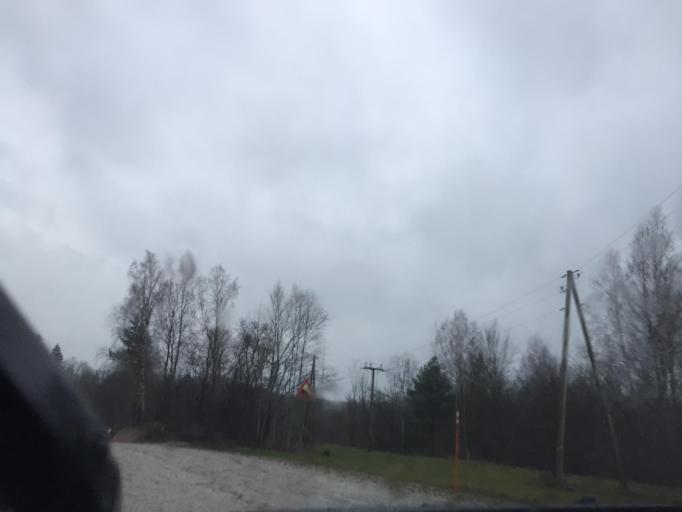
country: LV
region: Salacgrivas
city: Salacgriva
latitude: 57.7605
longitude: 24.4551
